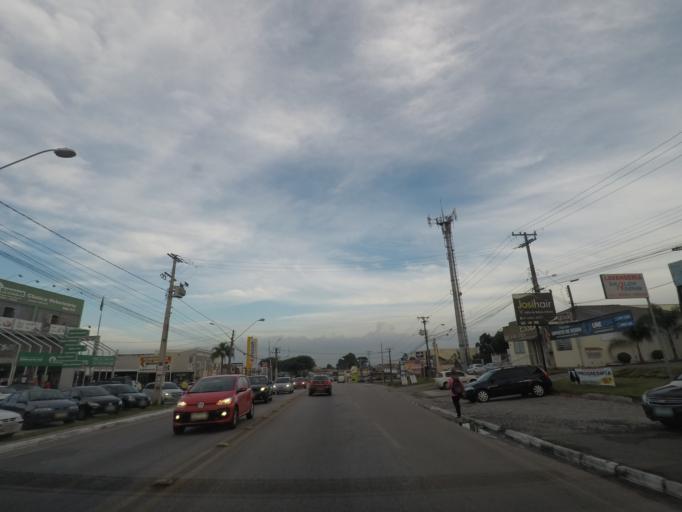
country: BR
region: Parana
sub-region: Colombo
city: Colombo
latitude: -25.3515
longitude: -49.2206
